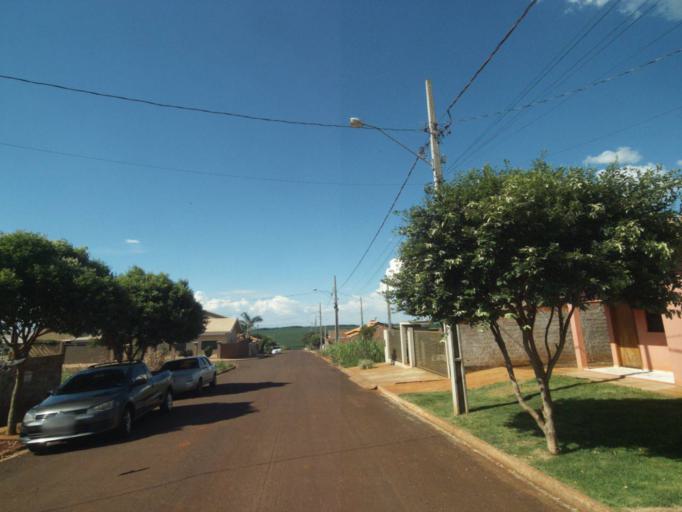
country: BR
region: Parana
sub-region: Sertanopolis
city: Sertanopolis
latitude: -23.0376
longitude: -50.8101
